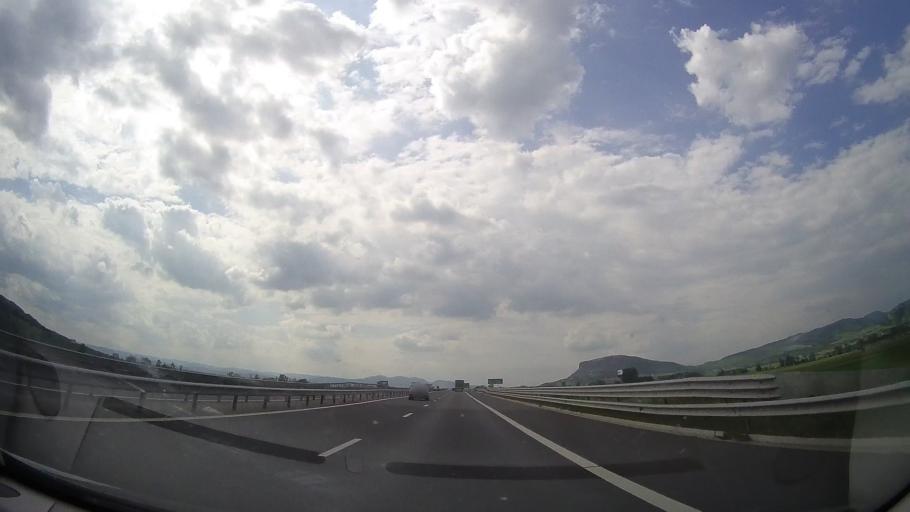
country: RO
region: Hunedoara
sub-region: Comuna Rapoltu Mare
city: Rapoltu Mare
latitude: 45.8426
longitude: 23.0779
